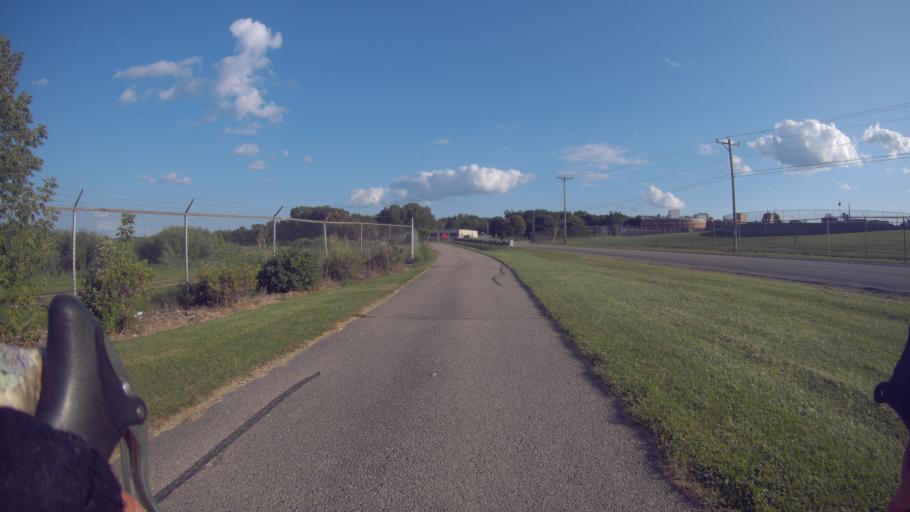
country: US
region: Wisconsin
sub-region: Dane County
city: Monona
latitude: 43.0354
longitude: -89.3541
